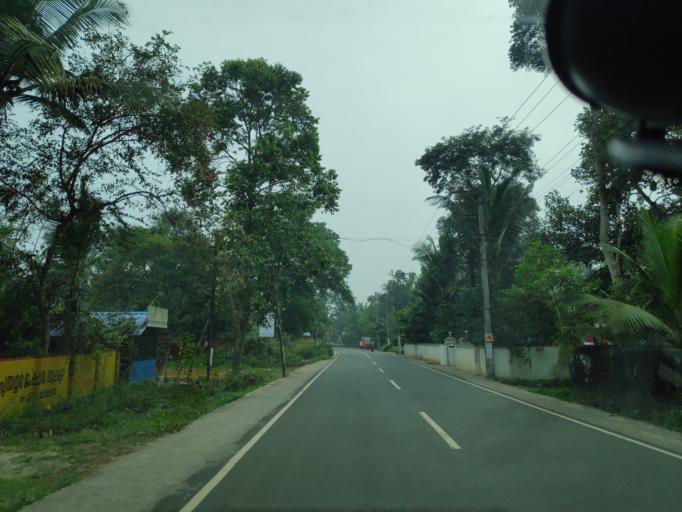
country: IN
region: Kerala
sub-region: Alappuzha
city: Shertallai
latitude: 9.6074
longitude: 76.3506
